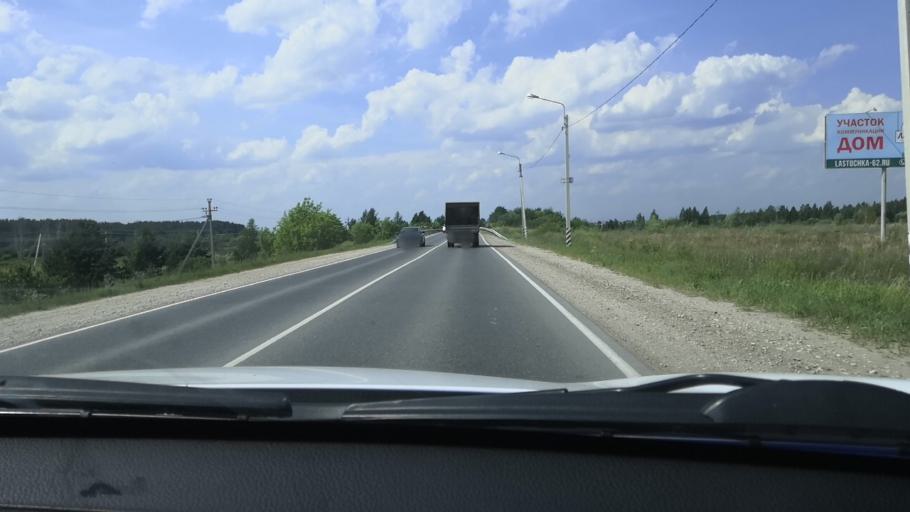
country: RU
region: Rjazan
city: Murmino
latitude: 54.6326
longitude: 39.9505
